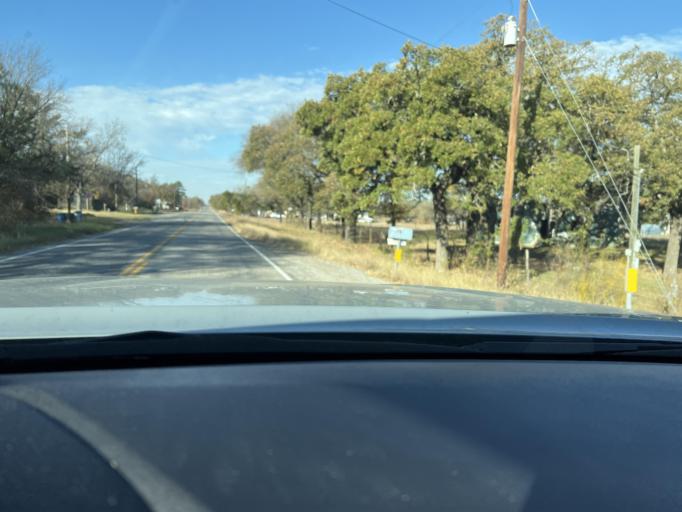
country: US
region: Texas
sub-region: Eastland County
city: Eastland
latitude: 32.4193
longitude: -98.7433
